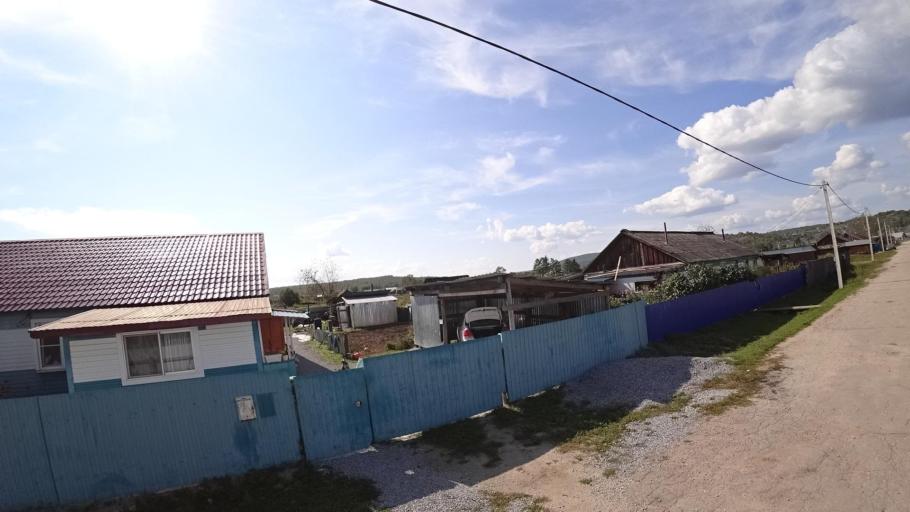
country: RU
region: Jewish Autonomous Oblast
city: Birakan
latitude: 48.9830
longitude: 131.7249
